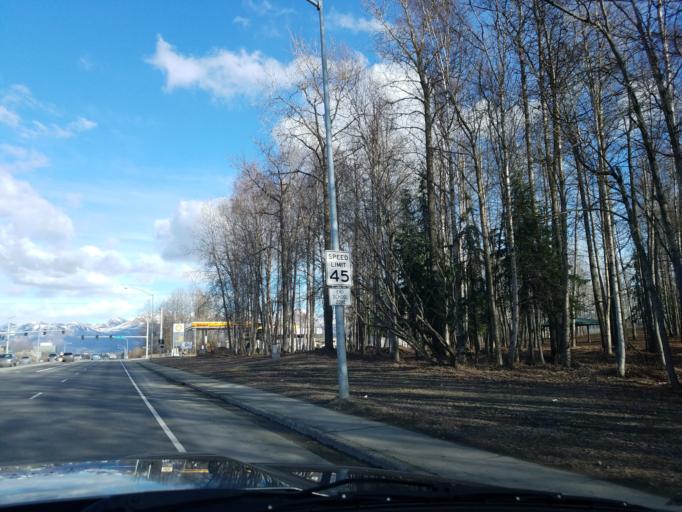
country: US
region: Alaska
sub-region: Anchorage Municipality
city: Anchorage
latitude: 61.1807
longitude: -149.9008
